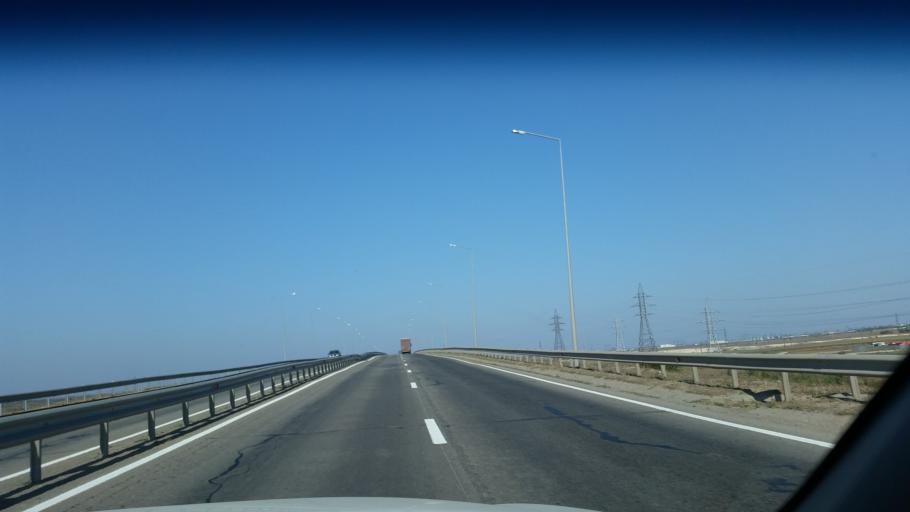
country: KZ
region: Astana Qalasy
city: Astana
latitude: 51.2245
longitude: 71.3237
